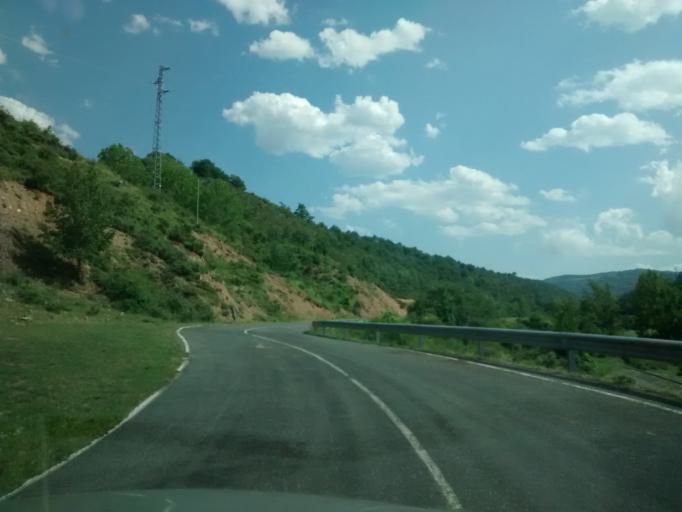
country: ES
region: La Rioja
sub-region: Provincia de La Rioja
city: Rabanera
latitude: 42.1857
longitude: -2.4838
